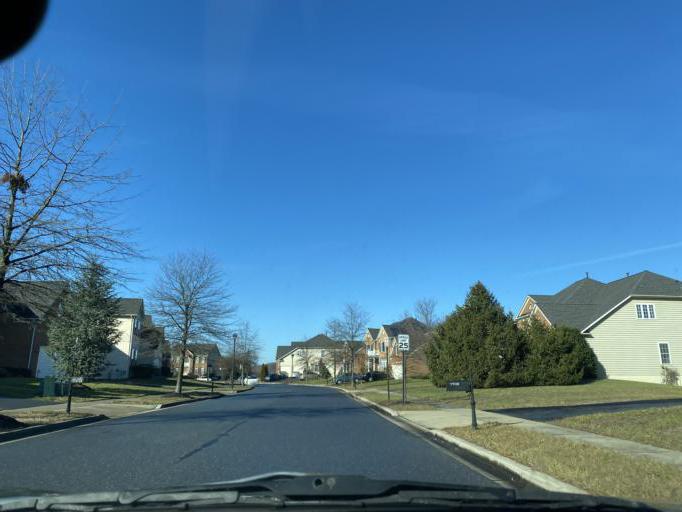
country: US
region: Maryland
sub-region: Prince George's County
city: Laurel
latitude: 39.0895
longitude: -76.8725
